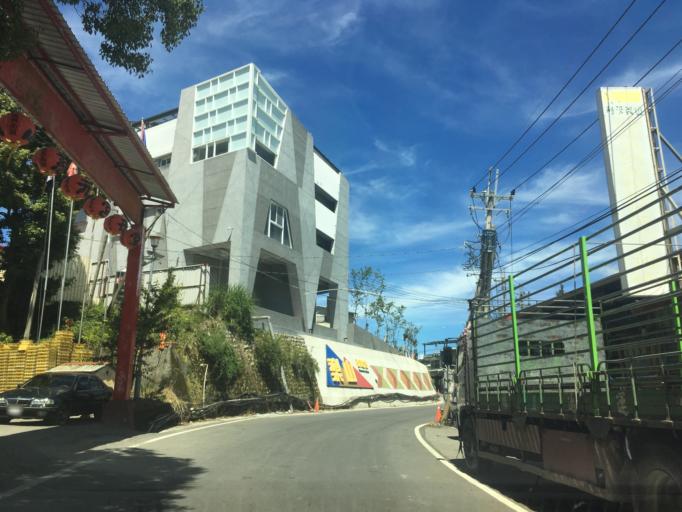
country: TW
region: Taiwan
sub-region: Nantou
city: Puli
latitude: 24.2578
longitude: 121.2631
